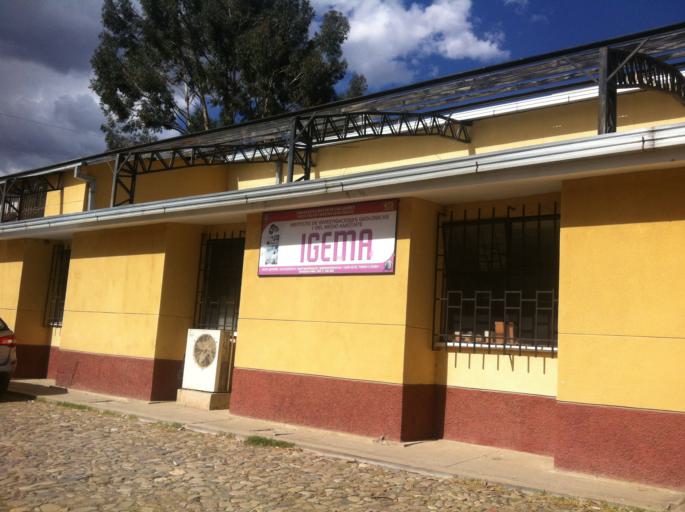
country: BO
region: La Paz
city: La Paz
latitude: -16.5384
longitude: -68.0680
